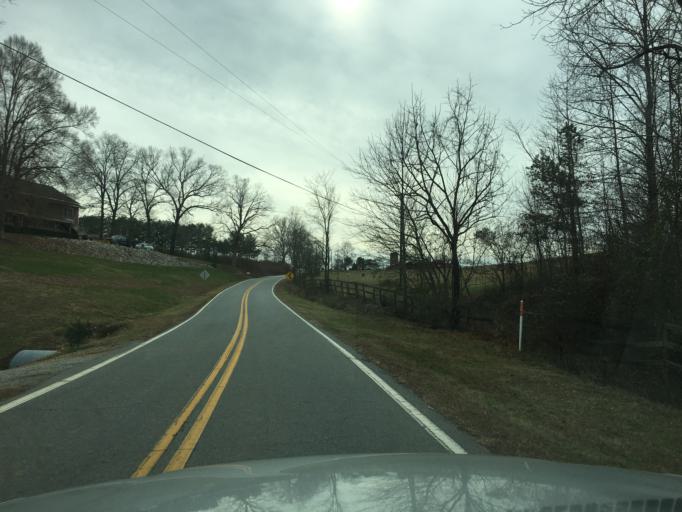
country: US
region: North Carolina
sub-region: McDowell County
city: West Marion
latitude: 35.6300
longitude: -81.9658
